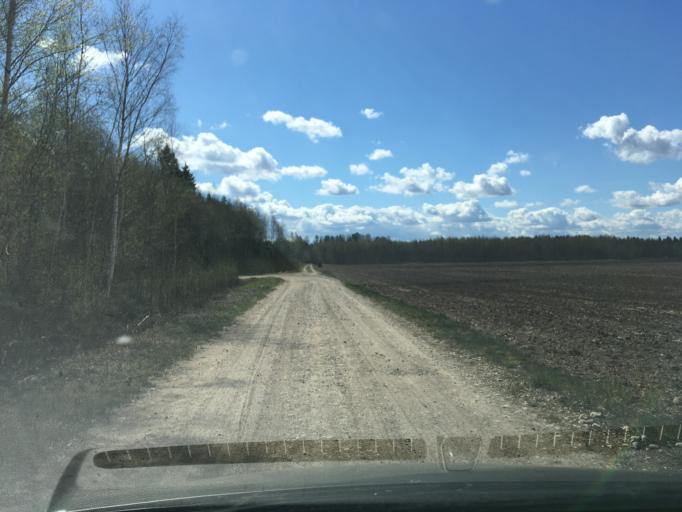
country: EE
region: Harju
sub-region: Raasiku vald
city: Raasiku
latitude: 59.2112
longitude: 25.1439
